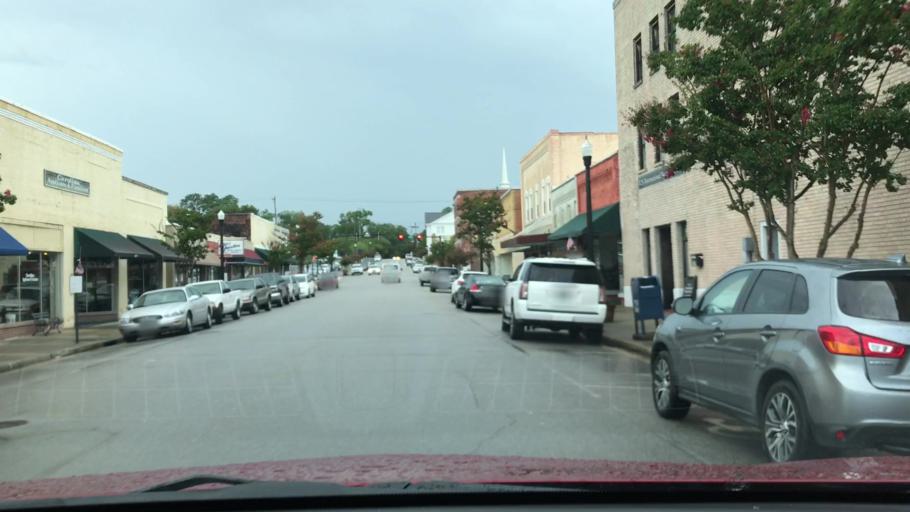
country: US
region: South Carolina
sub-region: Horry County
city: Conway
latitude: 33.8349
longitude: -79.0473
